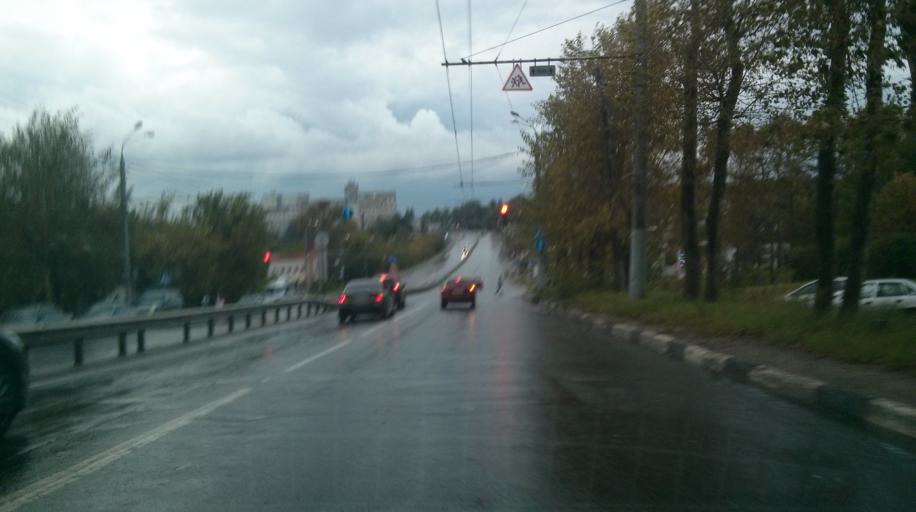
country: RU
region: Nizjnij Novgorod
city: Nizhniy Novgorod
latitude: 56.2870
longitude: 44.0364
